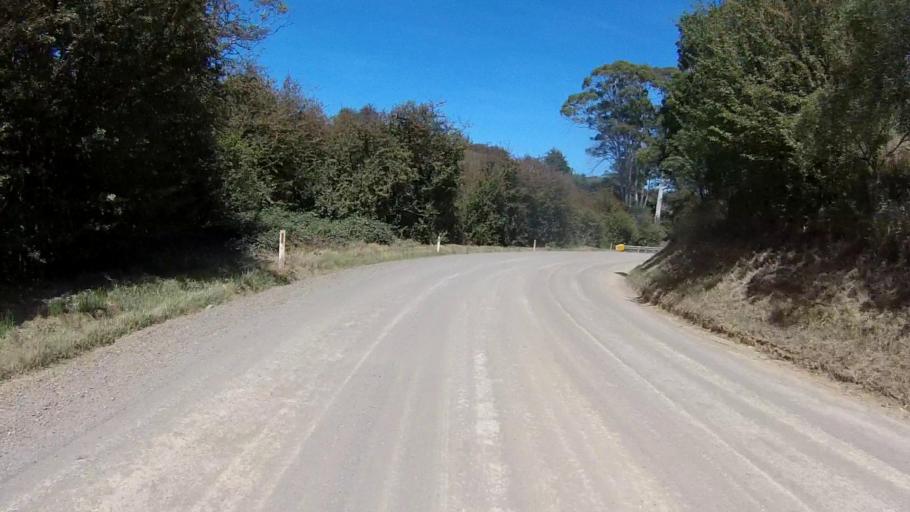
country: AU
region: Tasmania
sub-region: Sorell
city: Sorell
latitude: -42.7579
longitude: 147.6593
